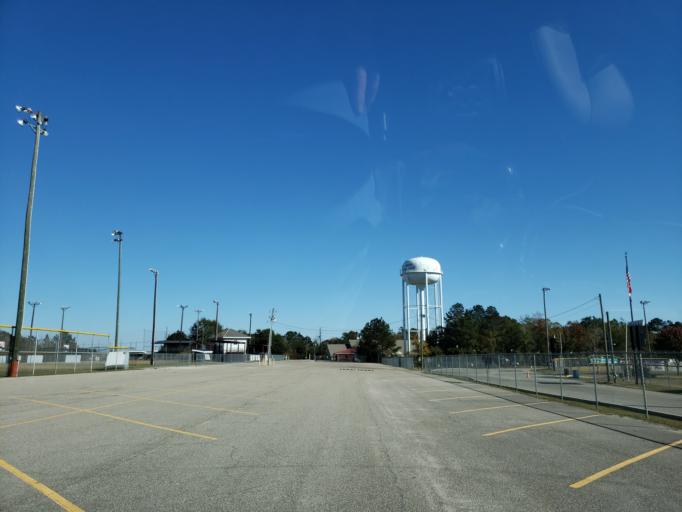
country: US
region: Mississippi
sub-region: Lamar County
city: West Hattiesburg
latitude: 31.3156
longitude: -89.4015
